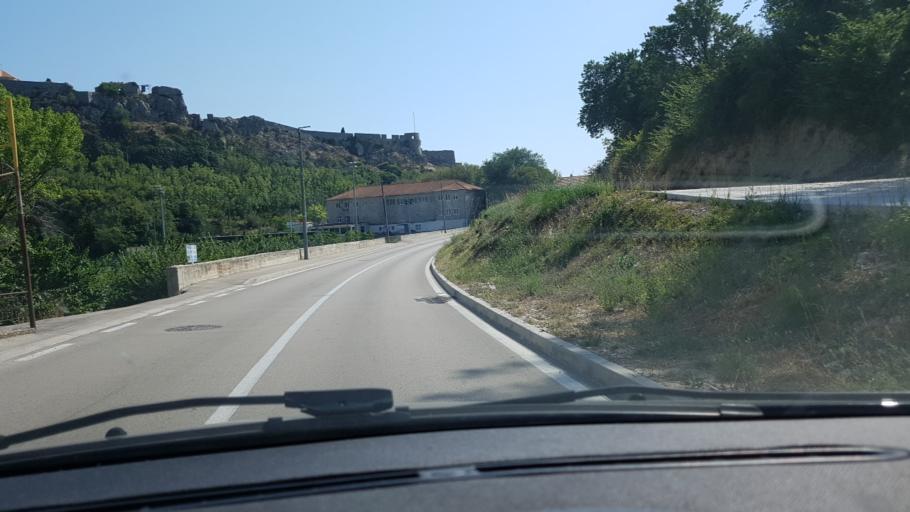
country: HR
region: Splitsko-Dalmatinska
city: Klis
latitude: 43.5626
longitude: 16.5242
